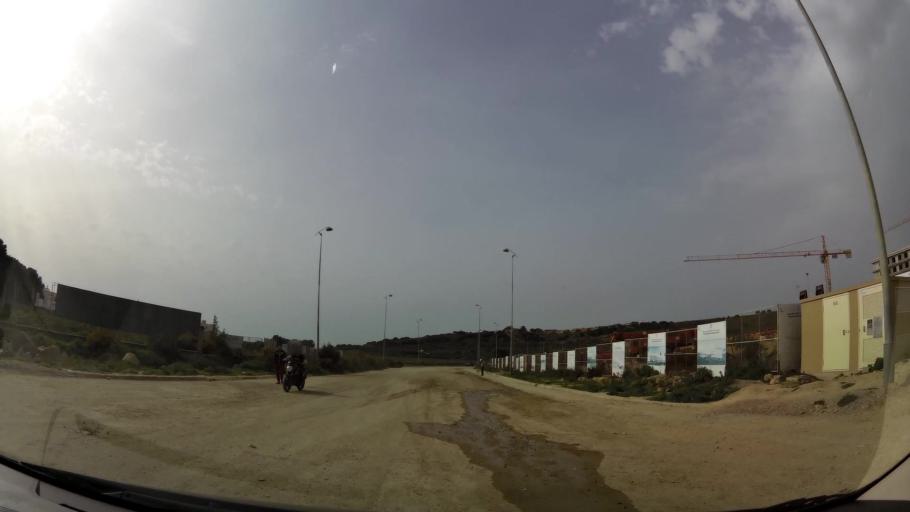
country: MA
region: Tanger-Tetouan
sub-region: Tanger-Assilah
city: Boukhalef
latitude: 35.6831
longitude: -5.9283
